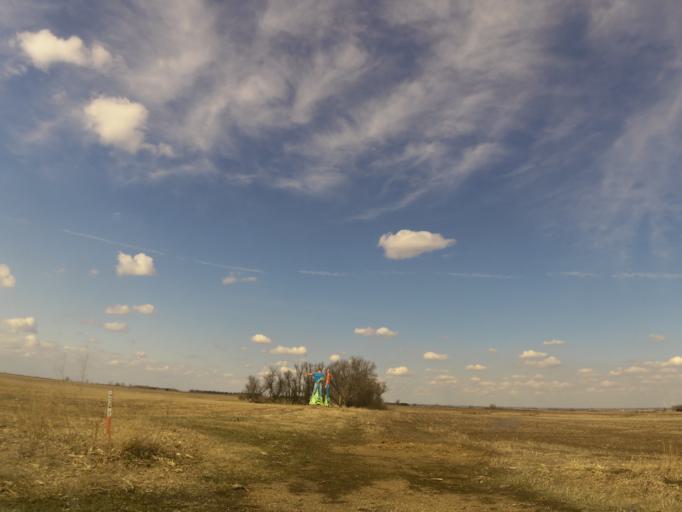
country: US
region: South Dakota
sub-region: Deuel County
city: Clear Lake
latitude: 44.9336
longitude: -96.5471
